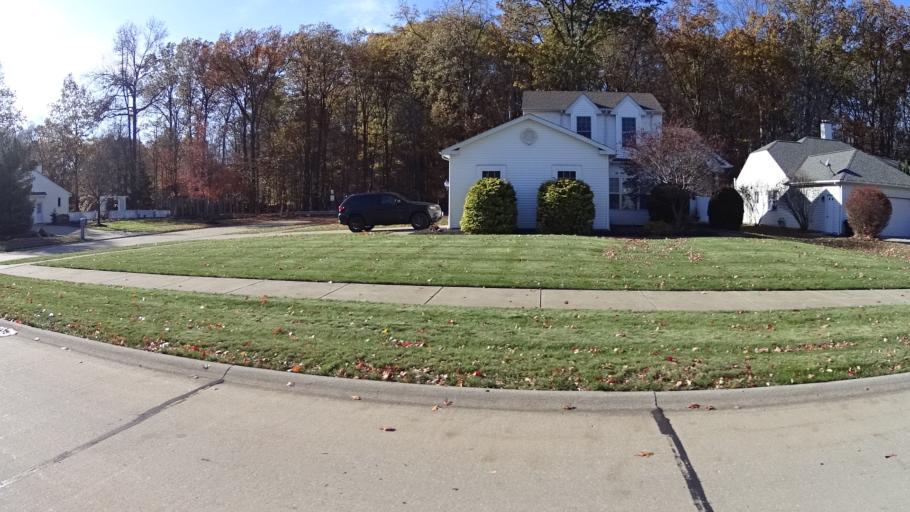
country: US
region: Ohio
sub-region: Lorain County
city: Avon Lake
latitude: 41.4971
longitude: -82.0080
